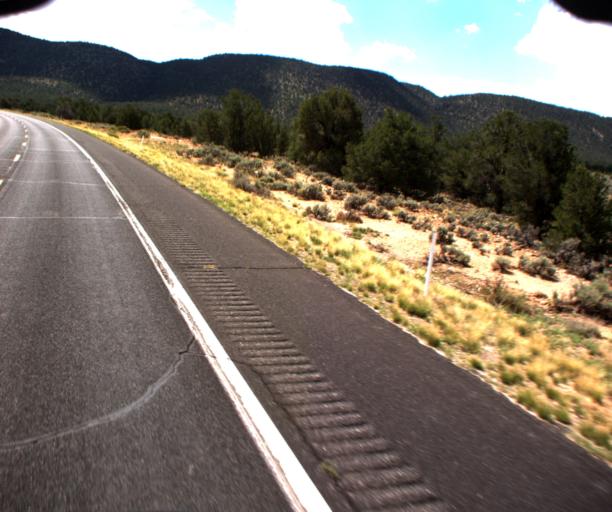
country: US
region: Arizona
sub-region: Coconino County
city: Grand Canyon
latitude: 35.9262
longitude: -111.7633
